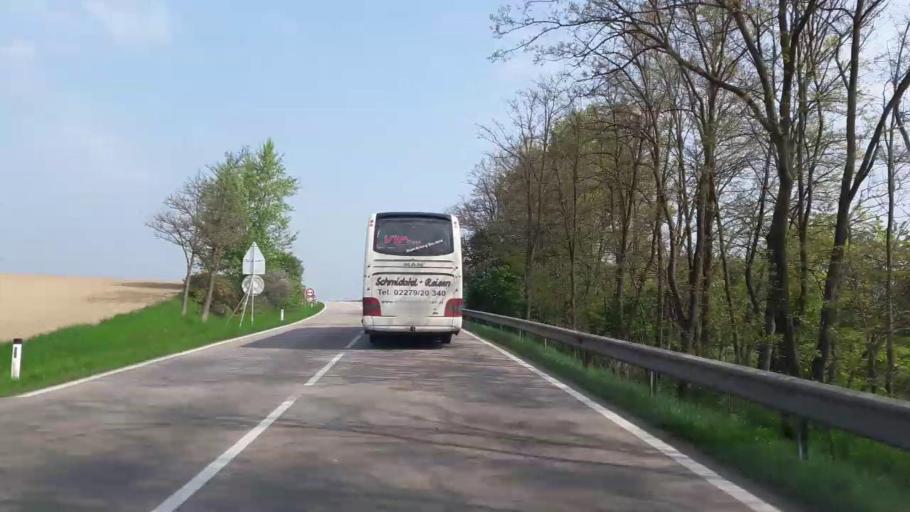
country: AT
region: Lower Austria
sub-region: Politischer Bezirk Hollabrunn
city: Wullersdorf
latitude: 48.6176
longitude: 16.0677
